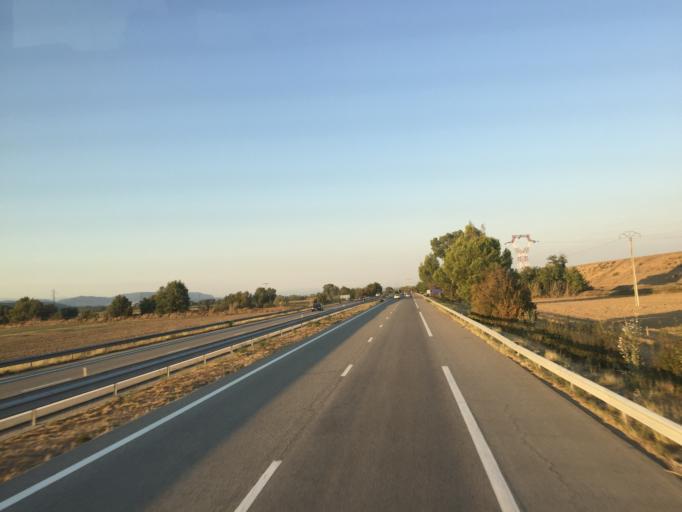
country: FR
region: Provence-Alpes-Cote d'Azur
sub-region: Departement des Alpes-de-Haute-Provence
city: Sainte-Tulle
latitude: 43.7356
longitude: 5.7506
